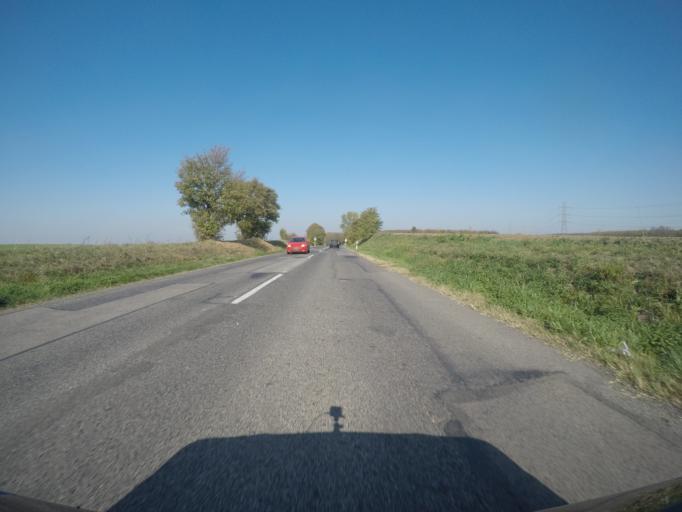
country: HU
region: Tolna
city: Szedres
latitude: 46.4543
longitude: 18.6867
